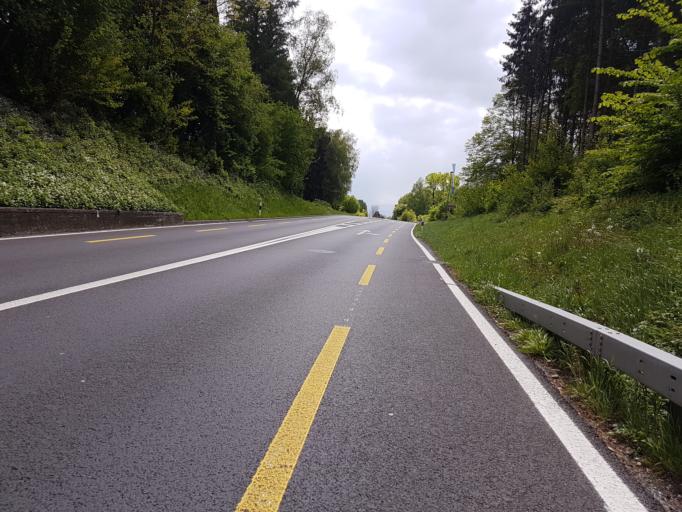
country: CH
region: Aargau
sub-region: Bezirk Brugg
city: Schinznach Bad
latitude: 47.4598
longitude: 8.1698
